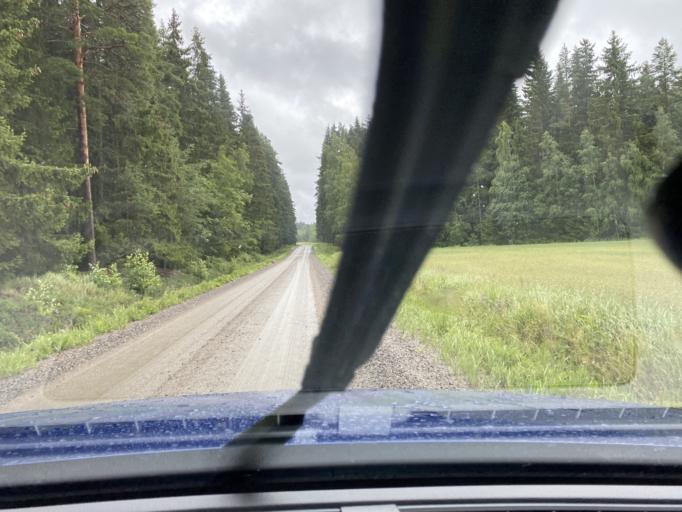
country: FI
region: Pirkanmaa
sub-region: Lounais-Pirkanmaa
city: Punkalaidun
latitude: 61.1489
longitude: 23.2366
